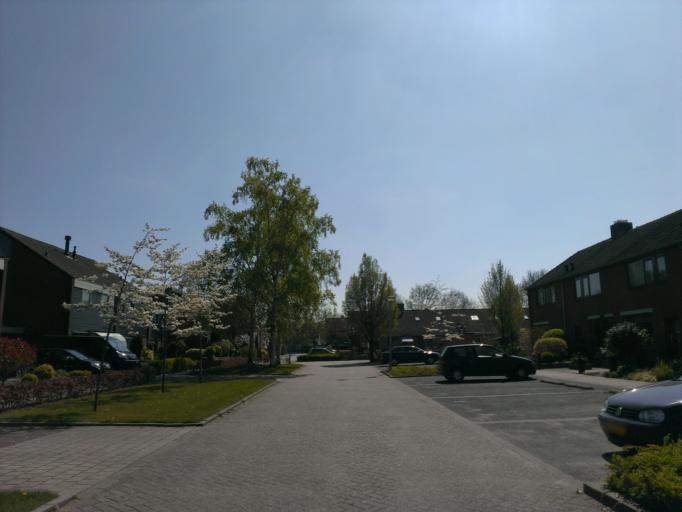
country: NL
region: Gelderland
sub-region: Gemeente Voorst
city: Twello
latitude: 52.2325
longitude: 6.0986
